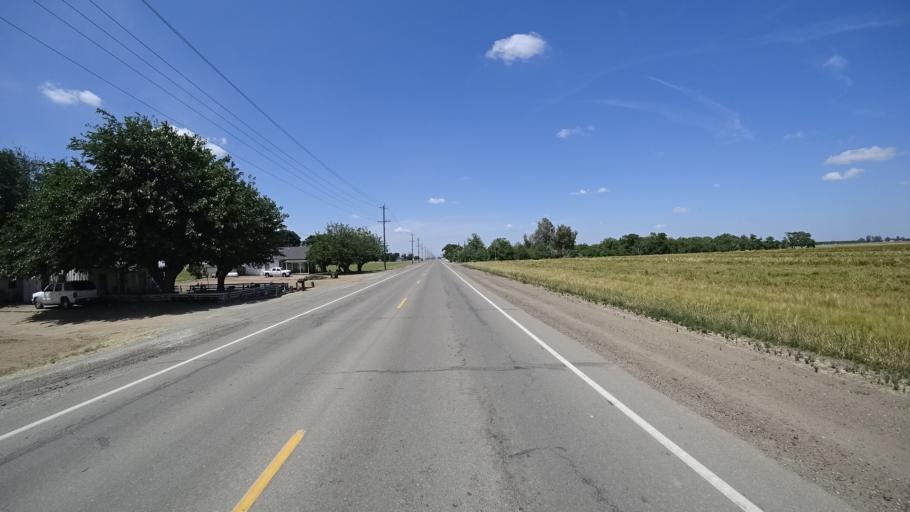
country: US
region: California
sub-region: Kings County
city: Home Garden
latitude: 36.2985
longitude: -119.5680
